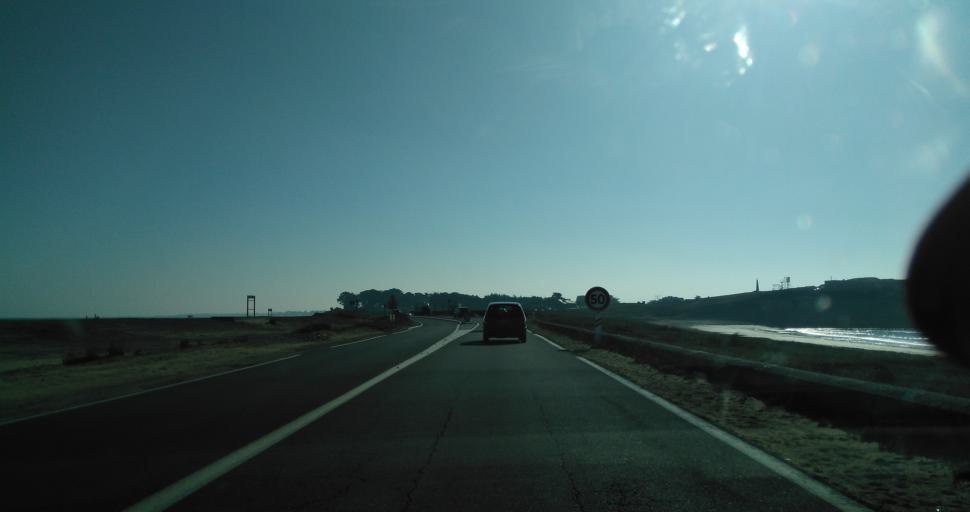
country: FR
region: Brittany
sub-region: Departement du Morbihan
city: Saint-Pierre-Quiberon
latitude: 47.5474
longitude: -3.1340
